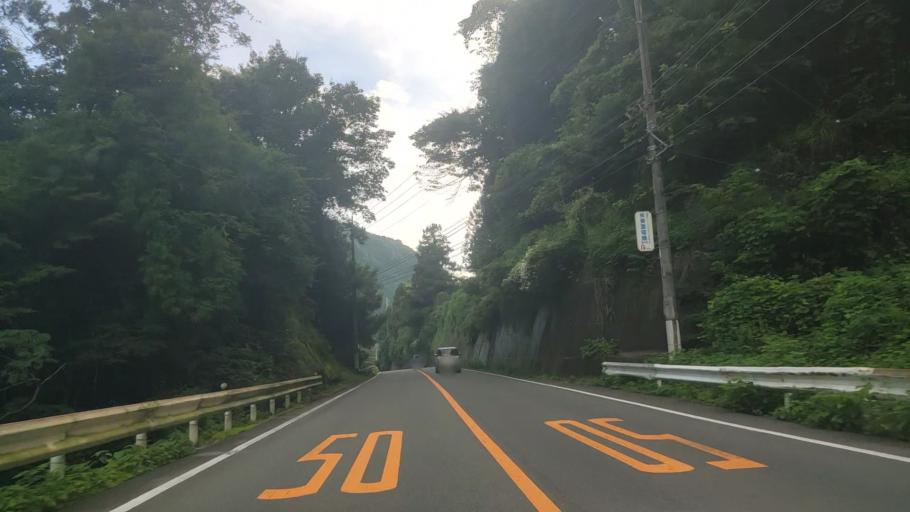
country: JP
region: Gunma
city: Omamacho-omama
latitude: 36.5034
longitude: 139.2928
